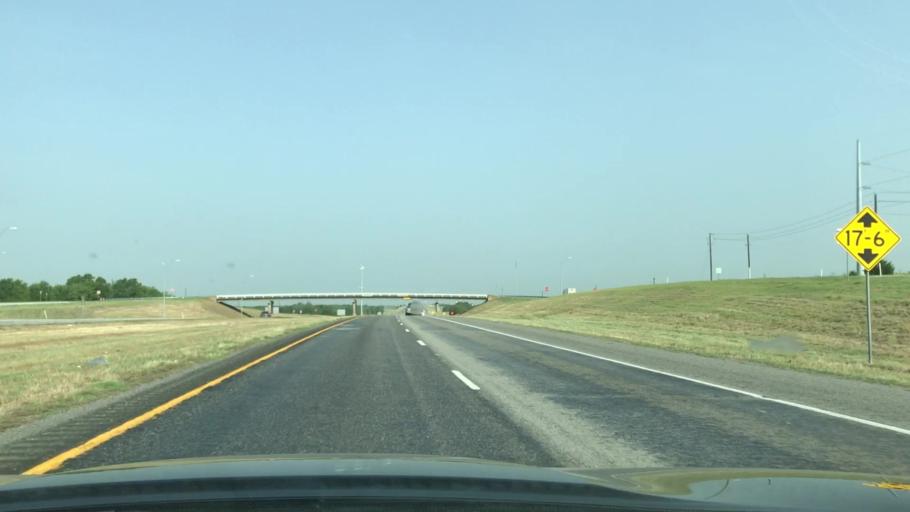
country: US
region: Texas
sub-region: Kaufman County
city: Terrell
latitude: 32.7287
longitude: -96.3375
